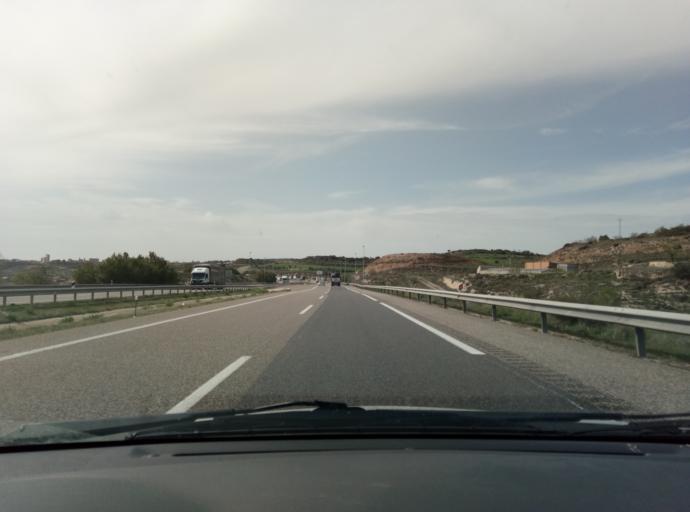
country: ES
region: Catalonia
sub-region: Provincia de Lleida
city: Cervera
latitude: 41.6623
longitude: 1.3063
